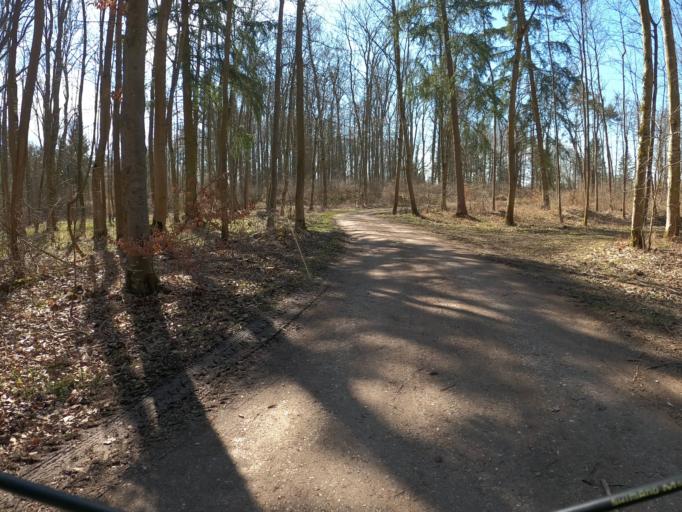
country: DE
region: Bavaria
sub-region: Swabia
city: Nersingen
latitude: 48.4372
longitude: 10.1457
